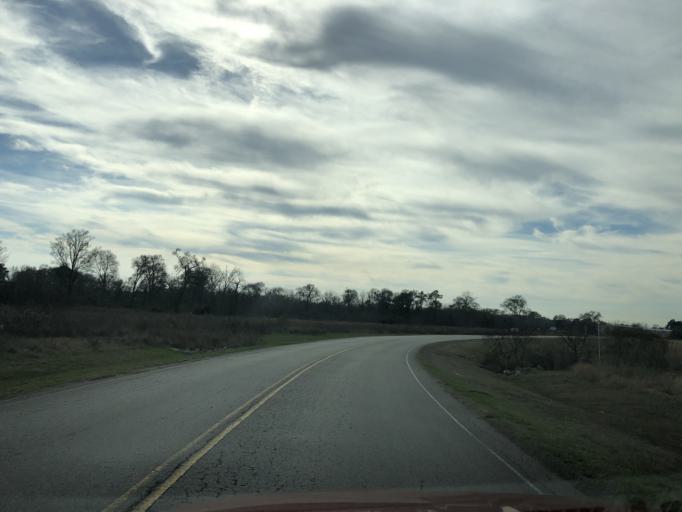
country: US
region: Texas
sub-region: Montgomery County
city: Panorama Village
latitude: 30.4028
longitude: -95.6927
